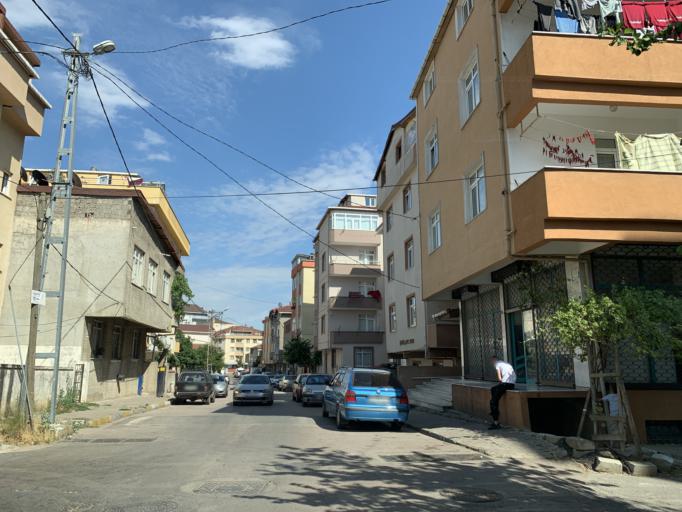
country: TR
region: Istanbul
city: Pendik
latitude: 40.8858
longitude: 29.2707
